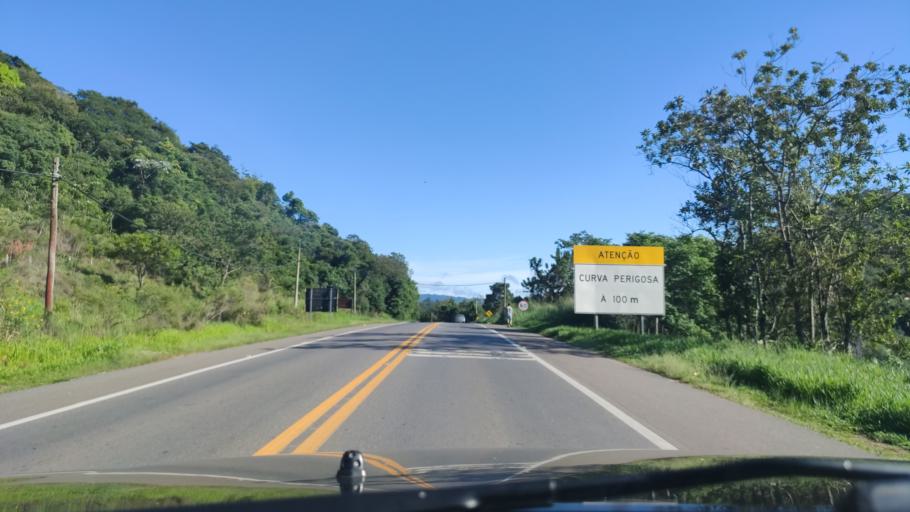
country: BR
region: Sao Paulo
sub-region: Socorro
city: Socorro
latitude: -22.5687
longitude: -46.5342
